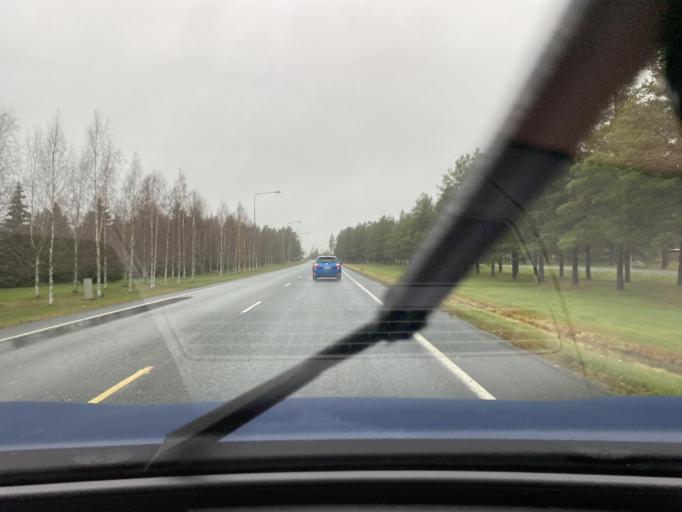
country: FI
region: Varsinais-Suomi
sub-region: Loimaa
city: Loimaa
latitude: 60.8617
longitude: 23.0244
